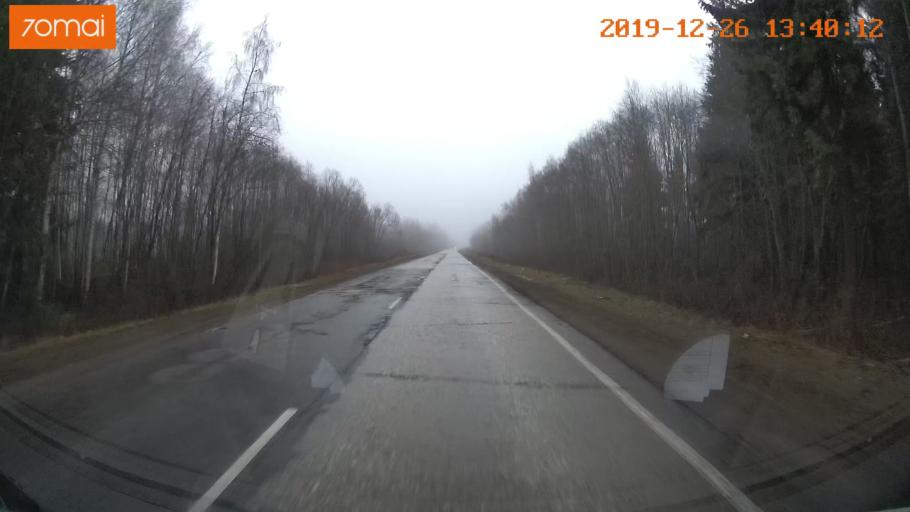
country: RU
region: Vologda
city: Sheksna
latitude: 58.7449
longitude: 38.4250
